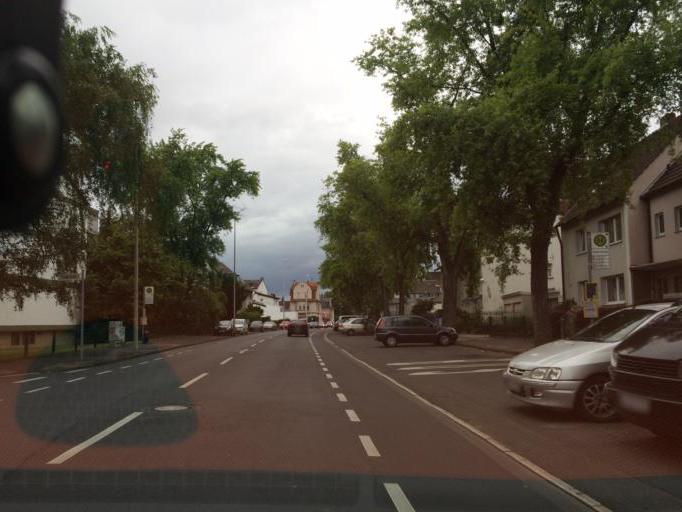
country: DE
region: North Rhine-Westphalia
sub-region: Regierungsbezirk Koln
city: Bonn
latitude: 50.6971
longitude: 7.1300
